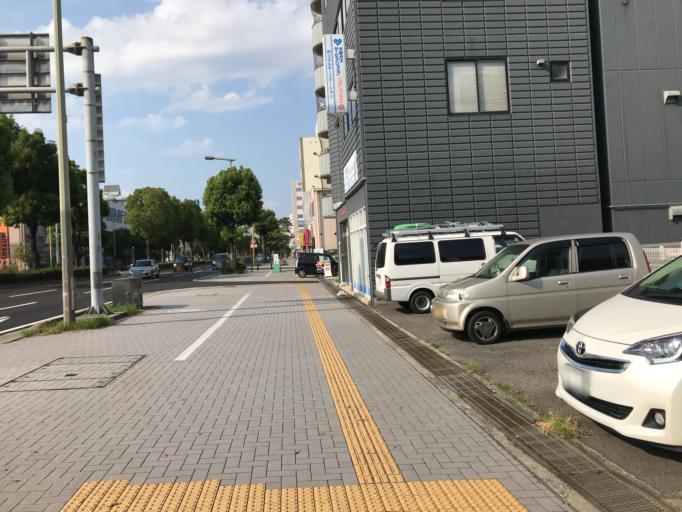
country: JP
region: Hyogo
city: Himeji
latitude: 34.8165
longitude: 134.6849
